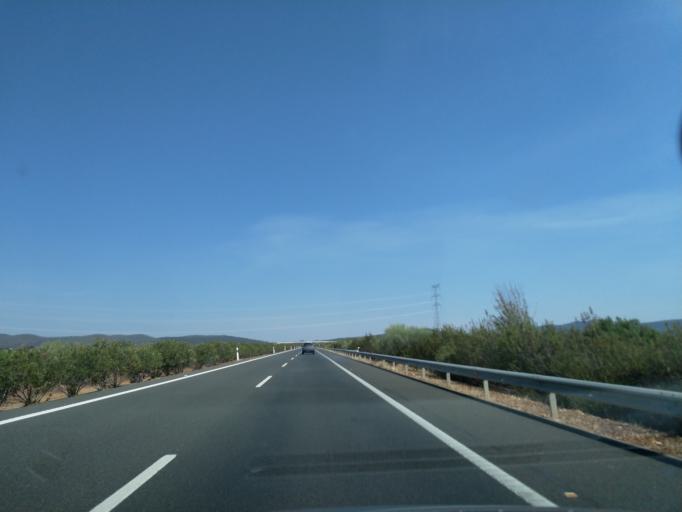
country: ES
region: Extremadura
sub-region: Provincia de Badajoz
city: Carmonita
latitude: 39.1226
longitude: -6.2776
